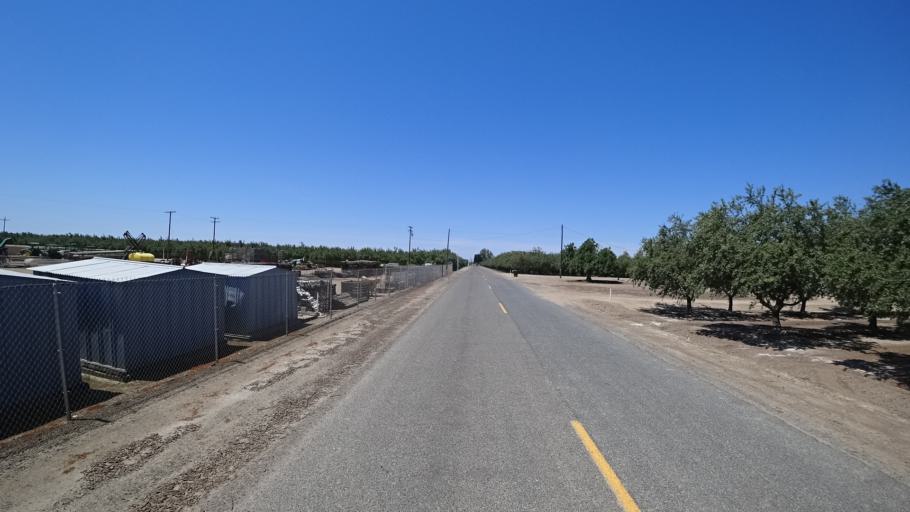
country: US
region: California
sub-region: Kings County
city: Armona
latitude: 36.3317
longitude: -119.7147
